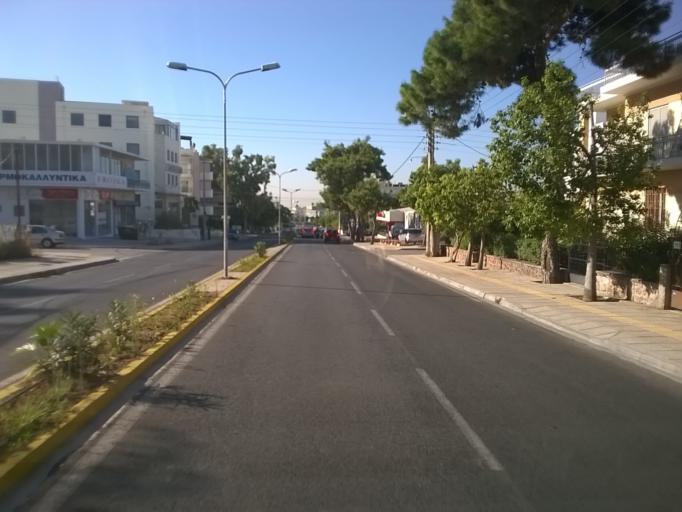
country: GR
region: Attica
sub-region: Nomarchia Athinas
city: Glyfada
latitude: 37.8783
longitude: 23.7579
